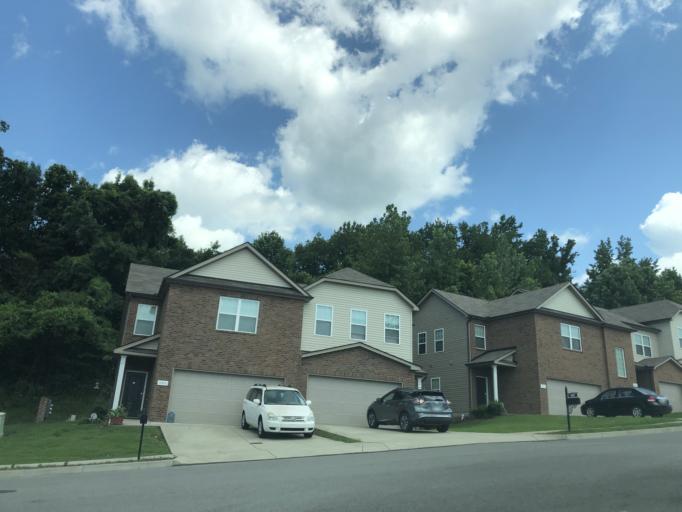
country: US
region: Tennessee
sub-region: Wilson County
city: Green Hill
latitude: 36.2141
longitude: -86.5863
